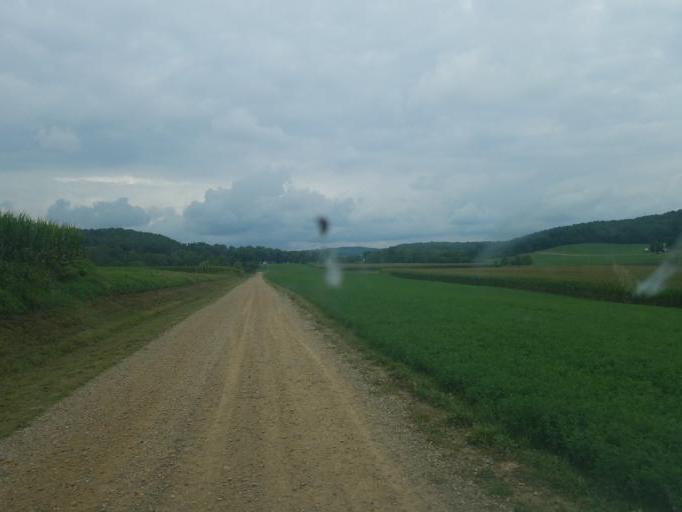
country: US
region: Ohio
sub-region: Knox County
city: Danville
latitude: 40.5252
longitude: -82.3051
